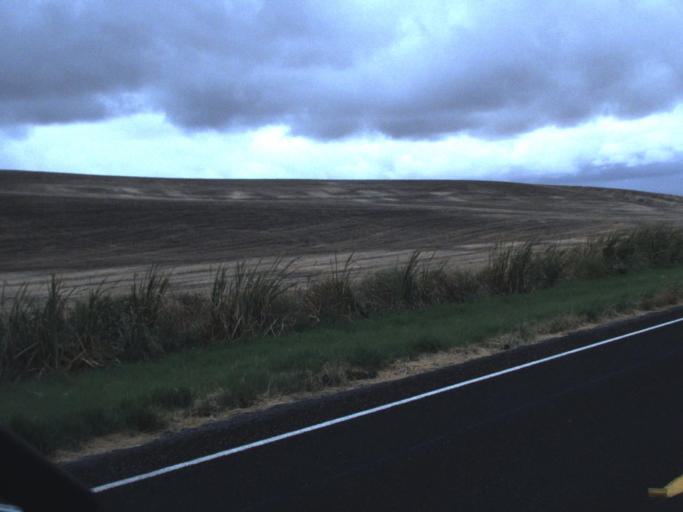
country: US
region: Washington
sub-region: Whitman County
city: Colfax
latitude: 47.1862
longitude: -117.3113
